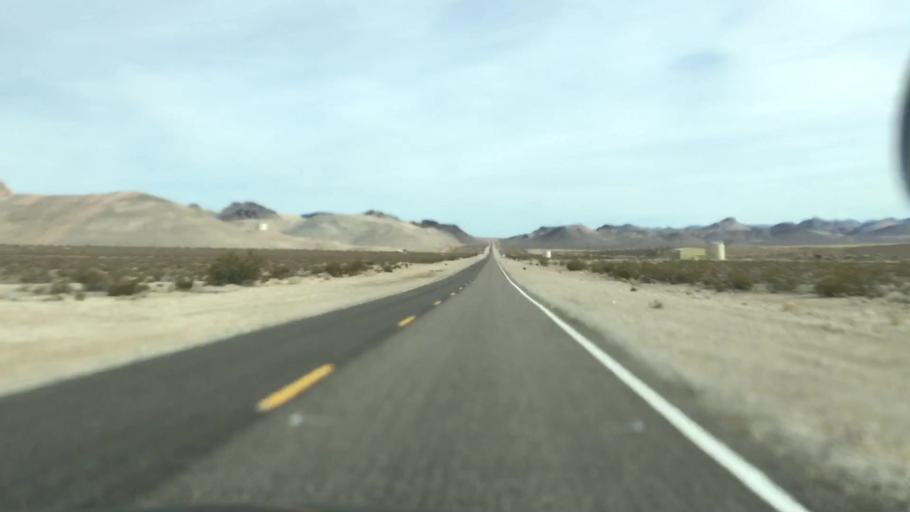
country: US
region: Nevada
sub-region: Nye County
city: Beatty
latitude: 36.8735
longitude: -116.8274
